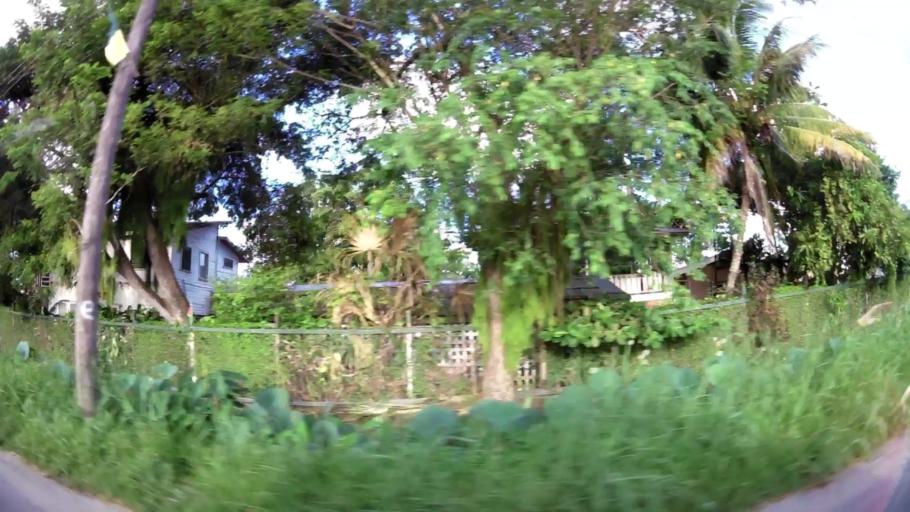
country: GY
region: Demerara-Mahaica
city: Georgetown
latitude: 6.8014
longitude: -58.1396
